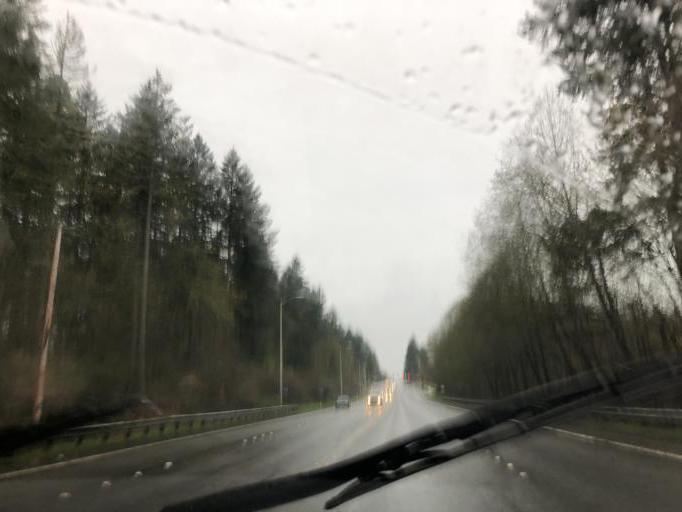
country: US
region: Washington
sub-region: Thurston County
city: Tanglewilde-Thompson Place
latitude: 47.0498
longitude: -122.8046
